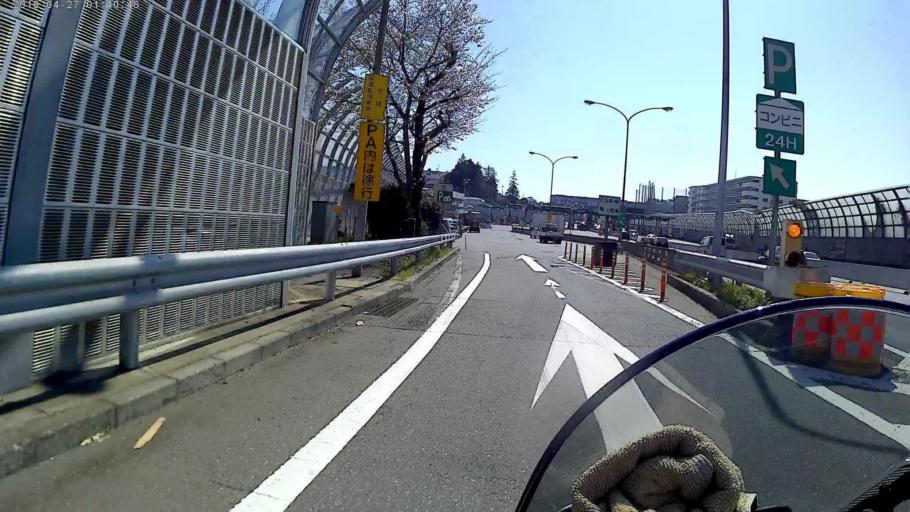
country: JP
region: Kanagawa
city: Yokohama
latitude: 35.4240
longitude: 139.5407
